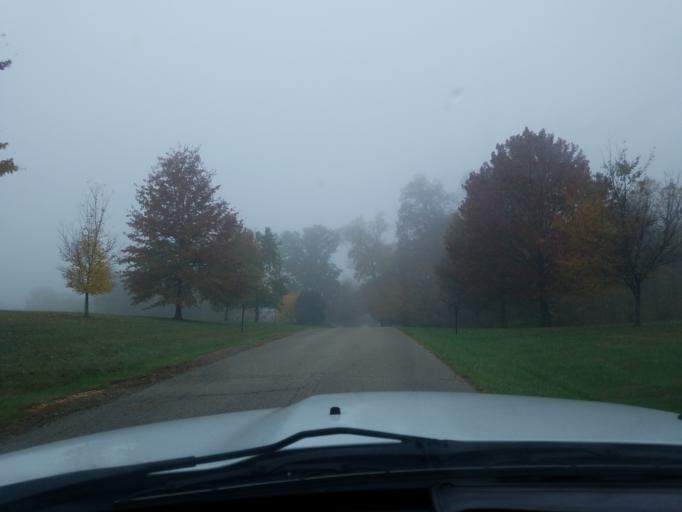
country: US
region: Indiana
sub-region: Floyd County
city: Galena
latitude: 38.3351
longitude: -85.9003
